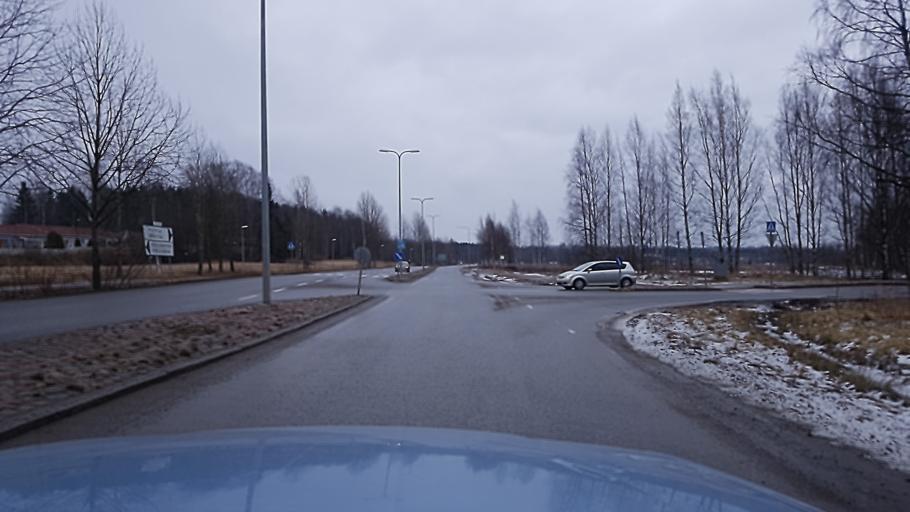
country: FI
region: Uusimaa
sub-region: Helsinki
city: Vantaa
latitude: 60.2658
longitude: 25.0413
